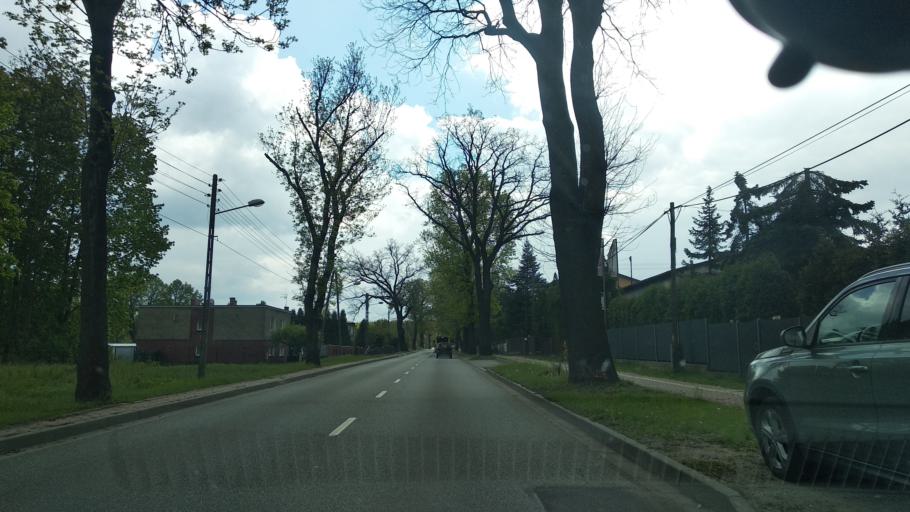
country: PL
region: Silesian Voivodeship
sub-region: Powiat mikolowski
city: Mikolow
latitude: 50.2265
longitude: 18.9240
